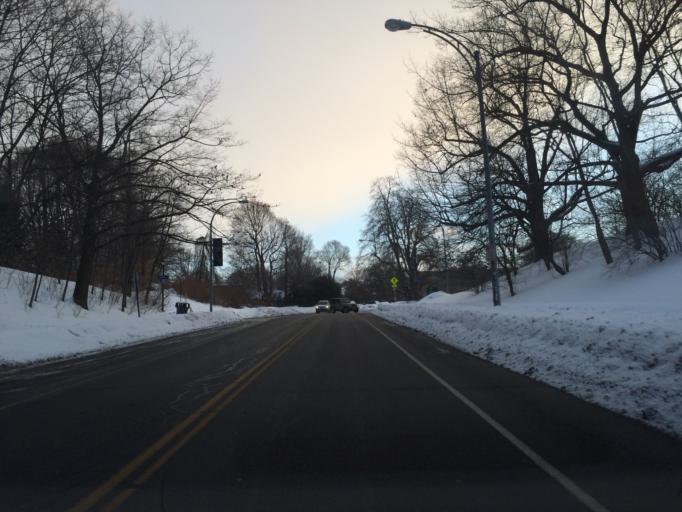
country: US
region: New York
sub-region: Monroe County
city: Rochester
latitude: 43.1337
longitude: -77.6081
